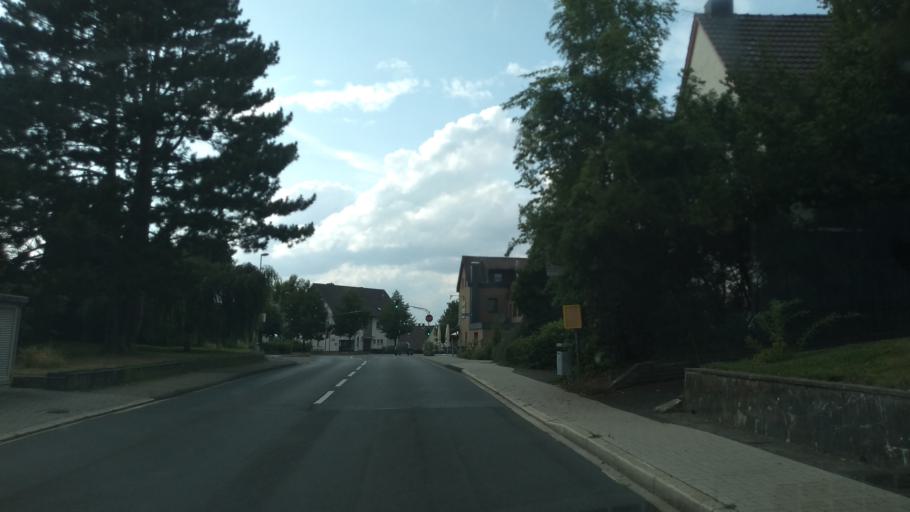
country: DE
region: North Rhine-Westphalia
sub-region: Regierungsbezirk Koln
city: Overath
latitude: 50.8699
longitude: 7.3246
